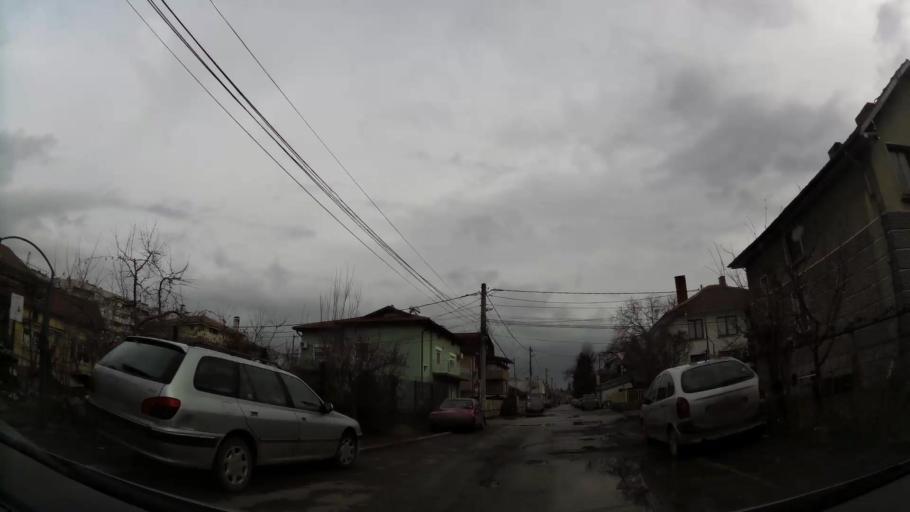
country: BG
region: Sofiya
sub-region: Obshtina Bozhurishte
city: Bozhurishte
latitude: 42.7448
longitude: 23.2681
